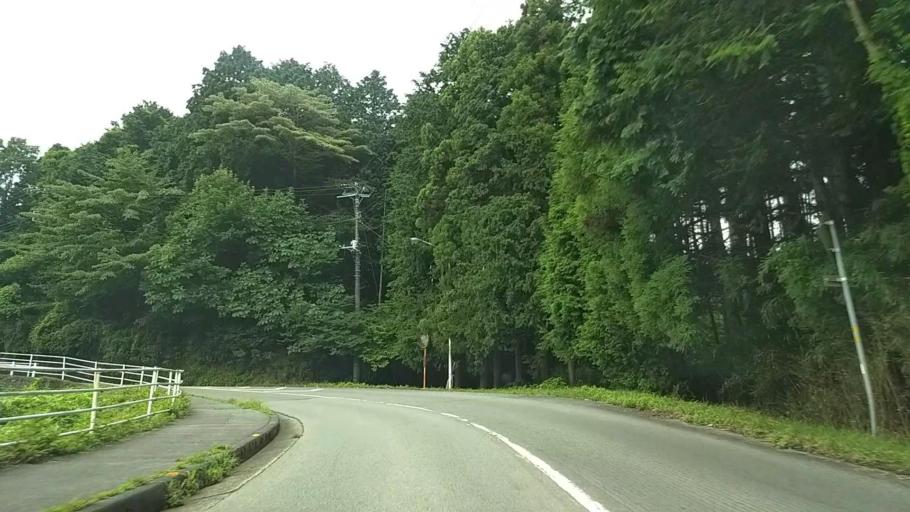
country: JP
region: Shizuoka
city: Gotemba
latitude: 35.3305
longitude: 138.9751
